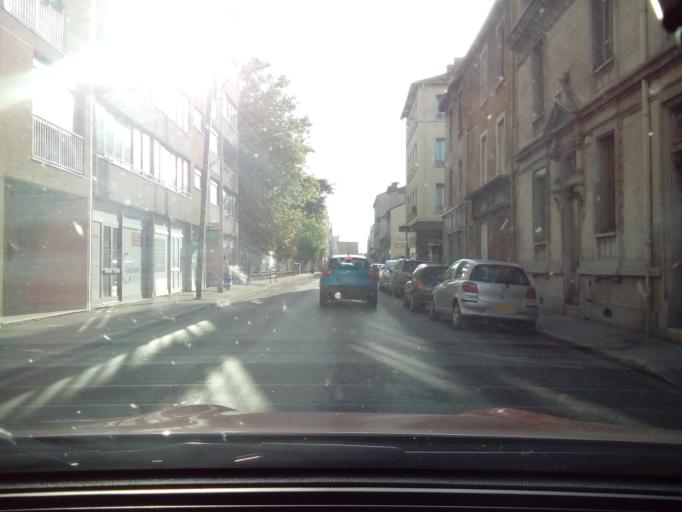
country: FR
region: Rhone-Alpes
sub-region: Departement du Rhone
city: Villeurbanne
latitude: 45.7598
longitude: 4.8947
